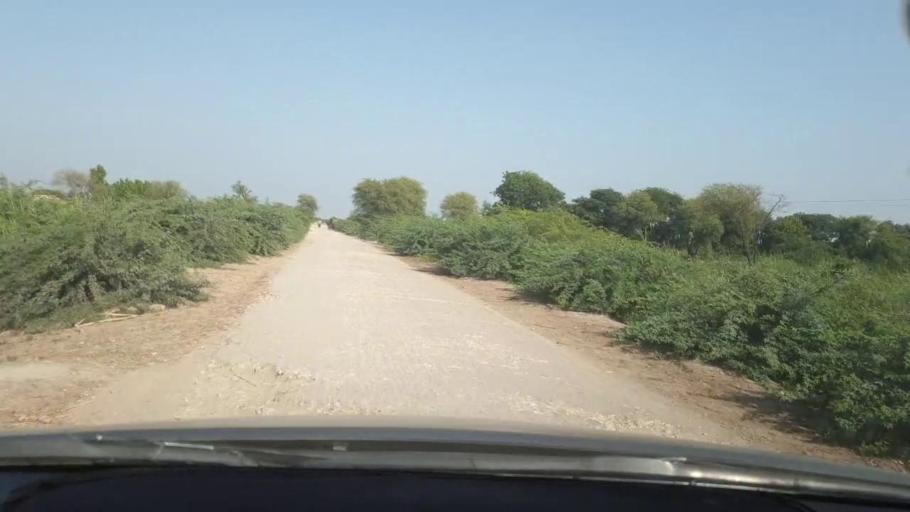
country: PK
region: Sindh
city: Naukot
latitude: 24.7610
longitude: 69.2129
